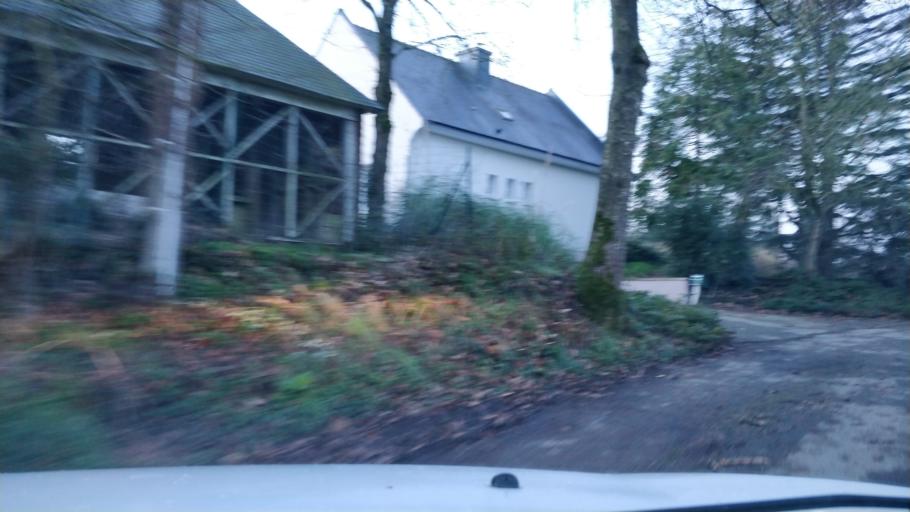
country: FR
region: Brittany
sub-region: Departement d'Ille-et-Vilaine
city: Louvigne-de-Bais
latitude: 48.0467
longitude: -1.3282
